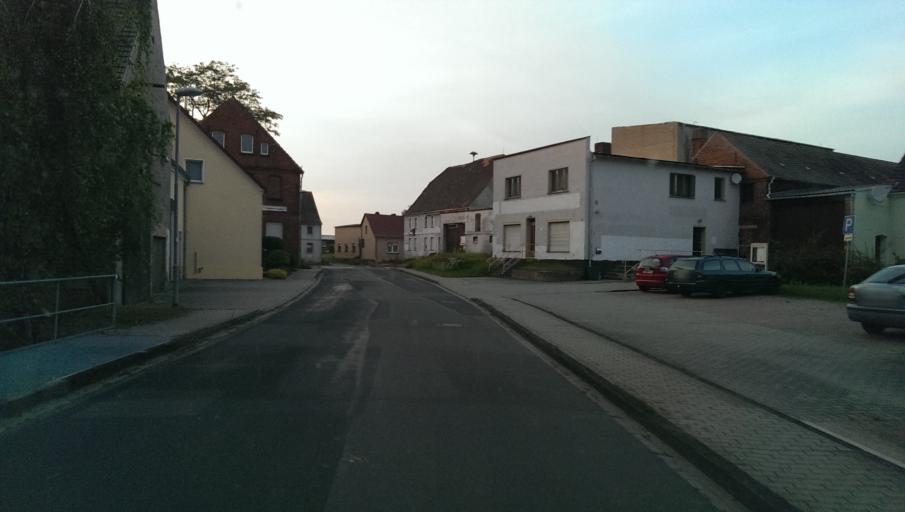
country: DE
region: Saxony-Anhalt
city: Kropstadt
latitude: 52.0015
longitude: 12.7789
